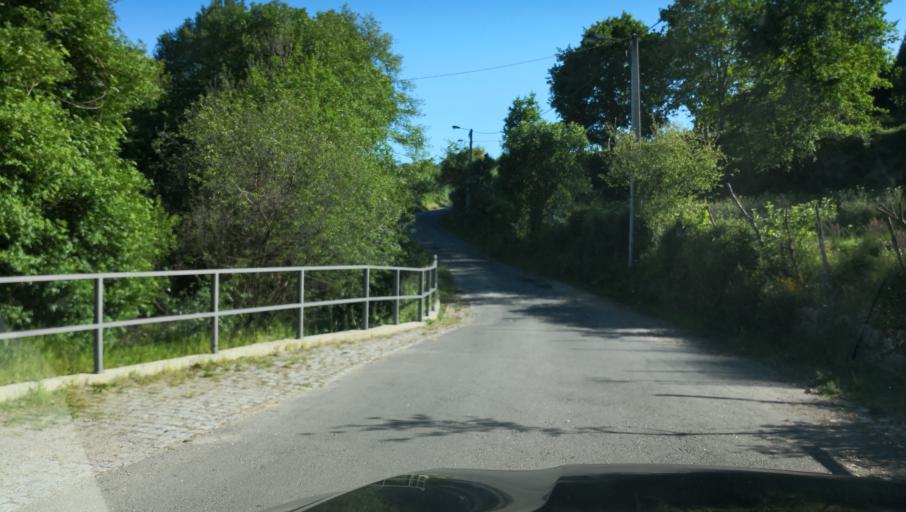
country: PT
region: Vila Real
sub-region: Vila Real
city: Vila Real
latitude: 41.3354
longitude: -7.7407
